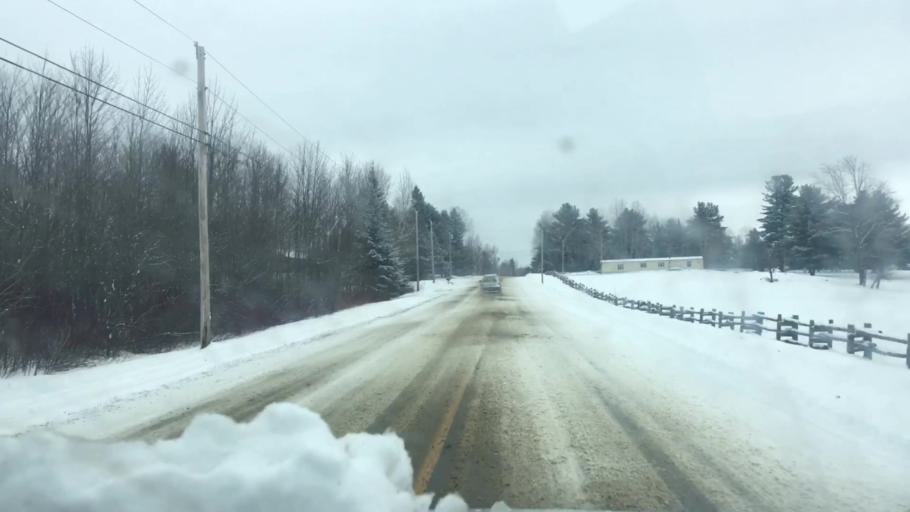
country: US
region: Maine
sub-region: Penobscot County
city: Bradford
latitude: 45.0318
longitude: -68.9465
